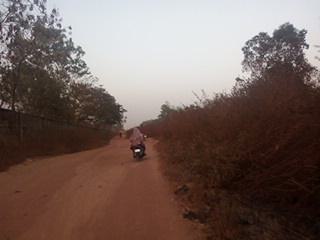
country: BJ
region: Borgou
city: Parakou
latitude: 9.3311
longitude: 2.5983
